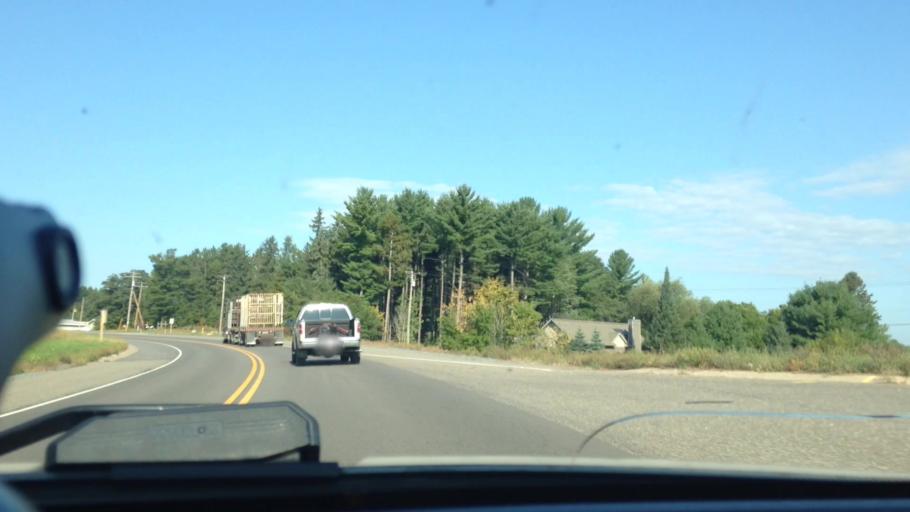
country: US
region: Michigan
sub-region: Dickinson County
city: Iron Mountain
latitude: 45.8754
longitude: -88.0867
